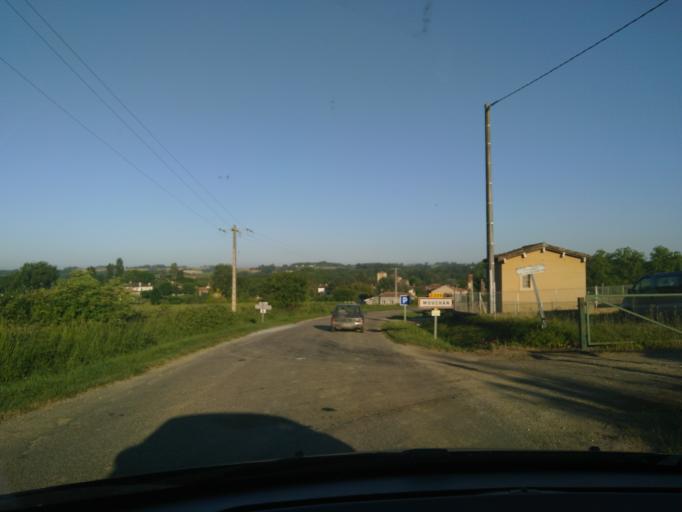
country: FR
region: Midi-Pyrenees
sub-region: Departement du Gers
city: Gondrin
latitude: 43.9036
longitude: 0.3027
